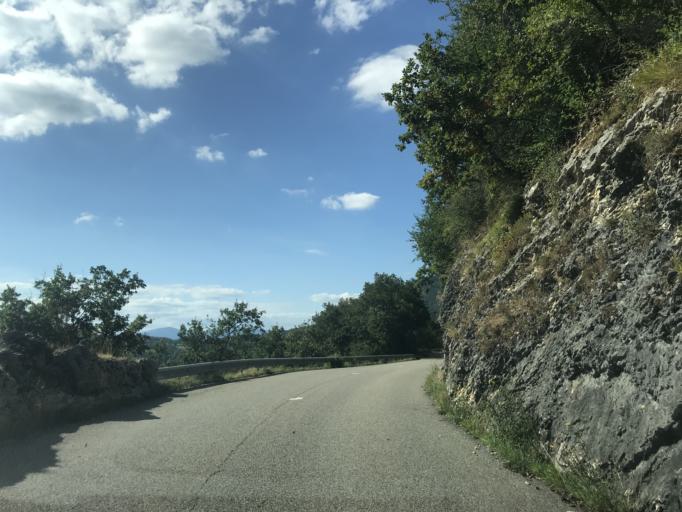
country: FR
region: Rhone-Alpes
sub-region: Departement de la Savoie
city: Le Bourget-du-Lac
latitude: 45.6967
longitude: 5.8342
